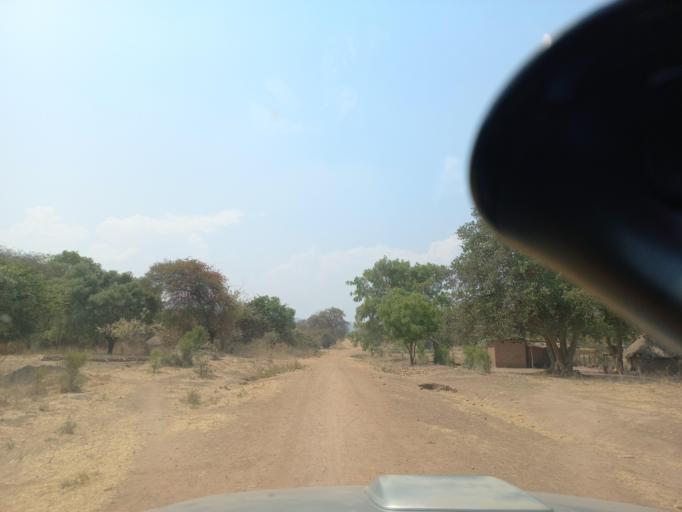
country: ZW
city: Chirundu
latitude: -15.9149
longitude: 28.6863
